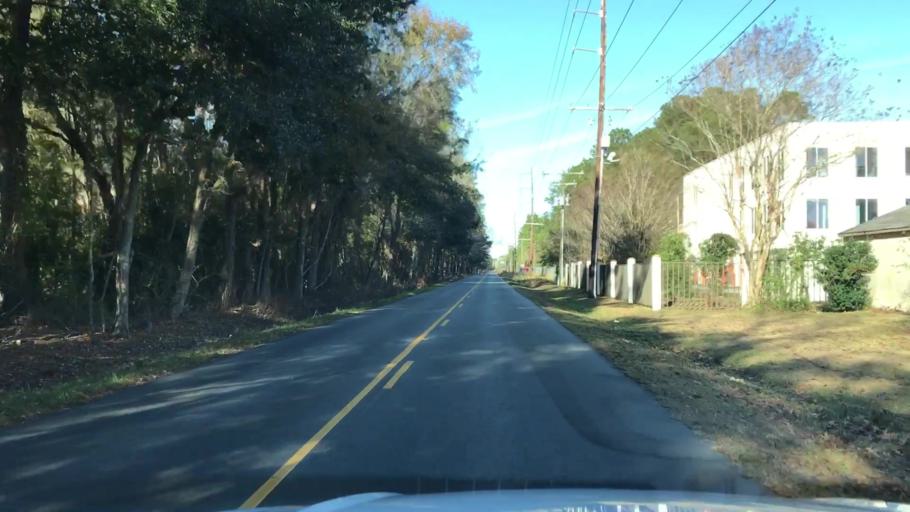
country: US
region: South Carolina
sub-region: Berkeley County
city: Ladson
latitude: 32.9865
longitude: -80.1113
